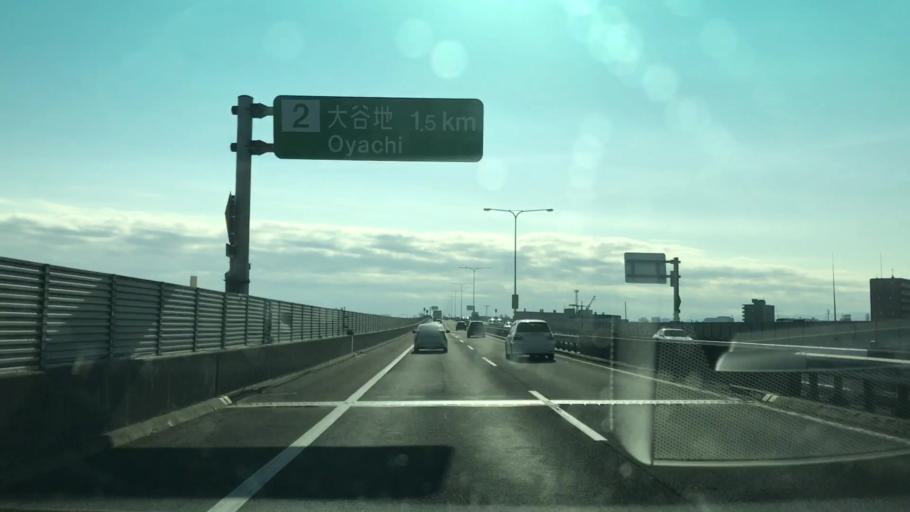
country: JP
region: Hokkaido
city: Sapporo
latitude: 43.0547
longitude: 141.4286
